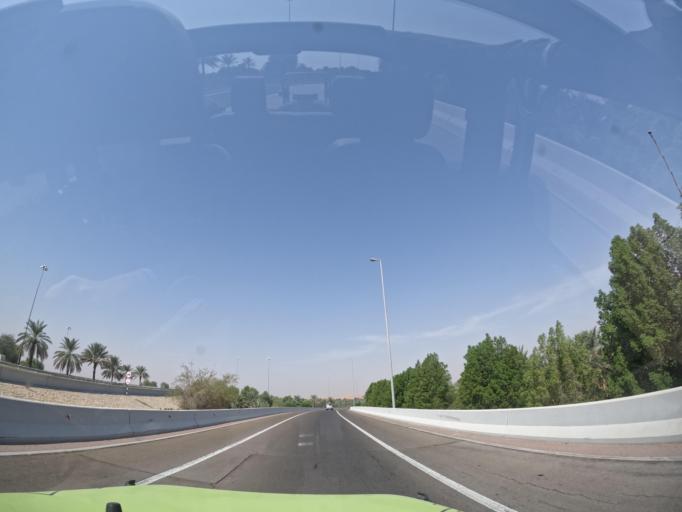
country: AE
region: Abu Dhabi
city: Al Ain
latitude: 24.2003
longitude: 55.5862
